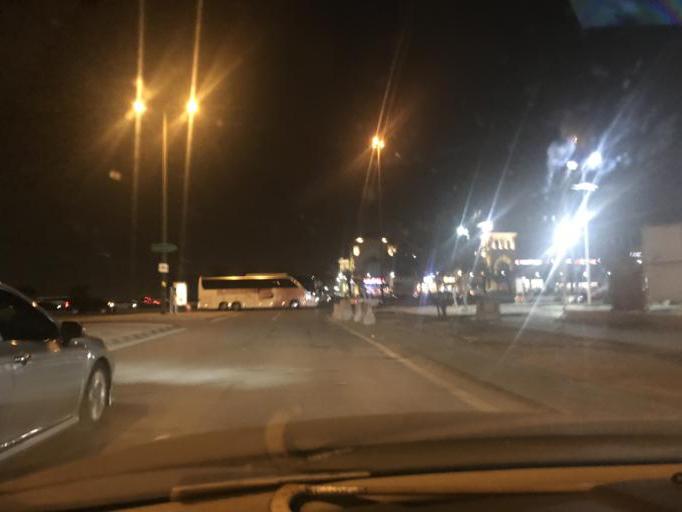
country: SA
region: Ar Riyad
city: Riyadh
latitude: 24.6745
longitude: 46.7803
